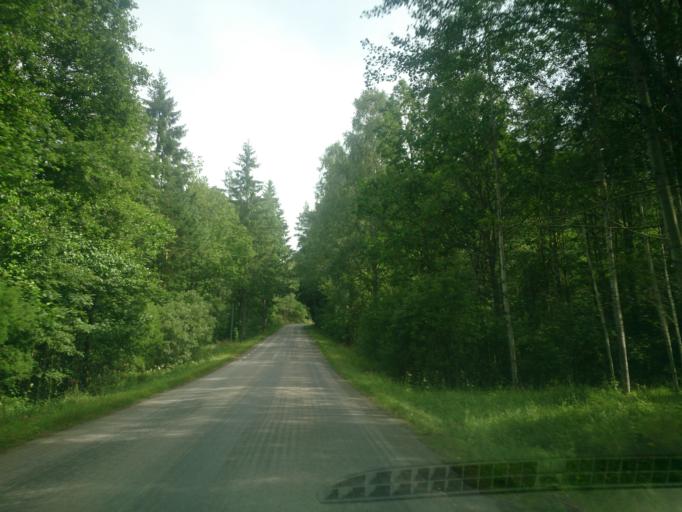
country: SE
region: OEstergoetland
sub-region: Soderkopings Kommun
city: Soederkoeping
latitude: 58.2842
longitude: 16.2324
